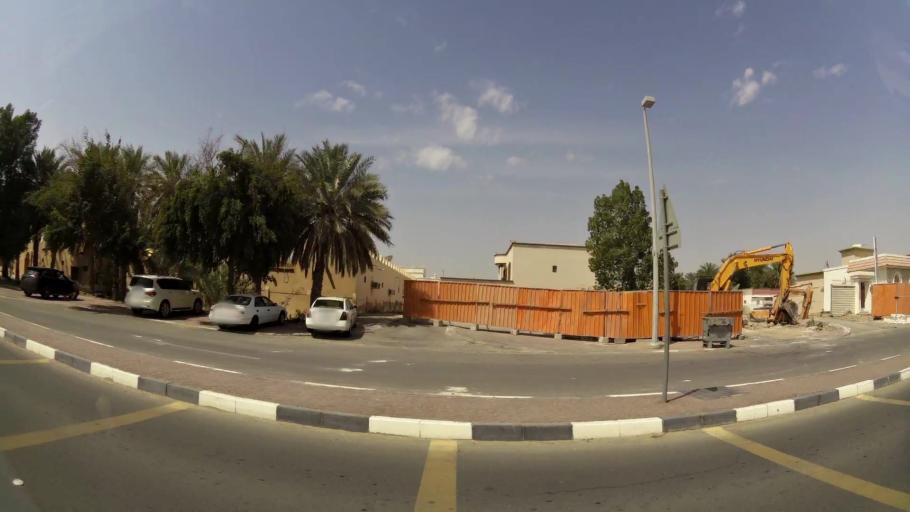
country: AE
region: Abu Dhabi
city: Abu Dhabi
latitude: 24.2952
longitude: 54.6439
